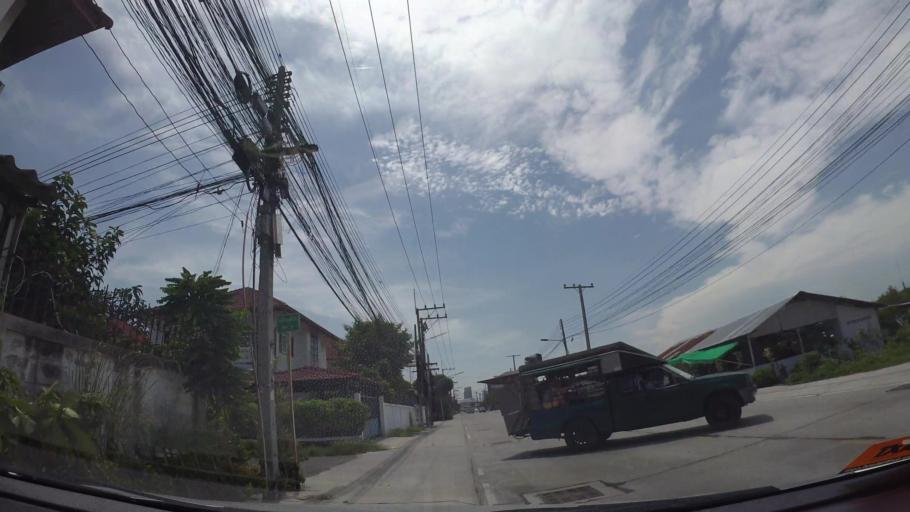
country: TH
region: Chon Buri
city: Chon Buri
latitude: 13.3345
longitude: 100.9486
